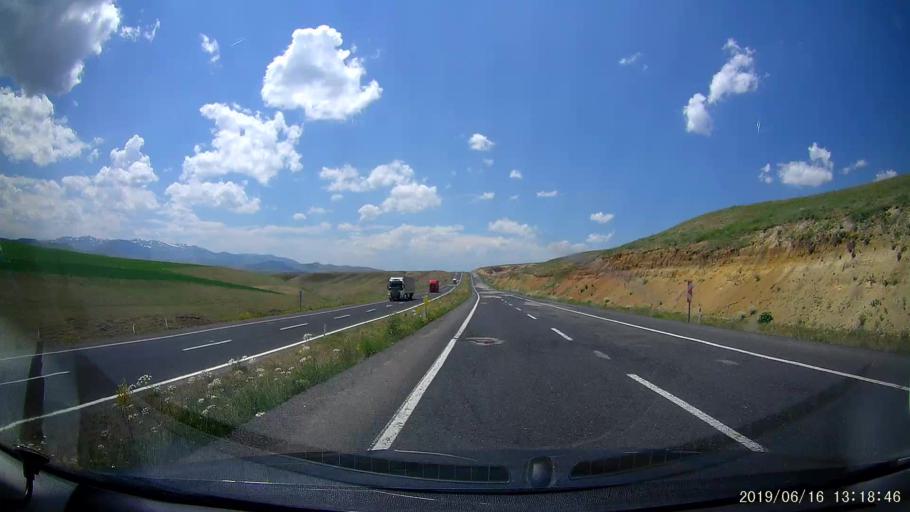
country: TR
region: Agri
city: Taslicay
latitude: 39.6319
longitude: 43.4237
